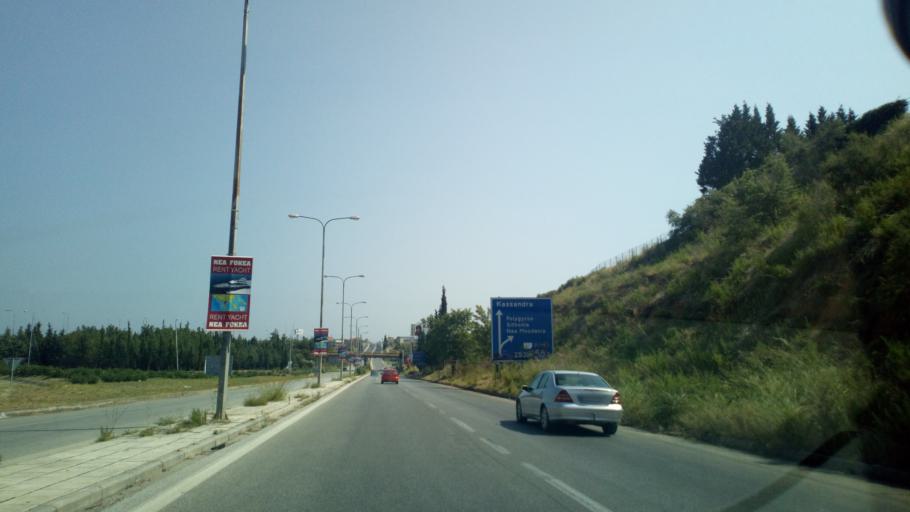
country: GR
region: Central Macedonia
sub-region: Nomos Chalkidikis
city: Nea Moudhania
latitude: 40.2447
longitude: 23.2972
